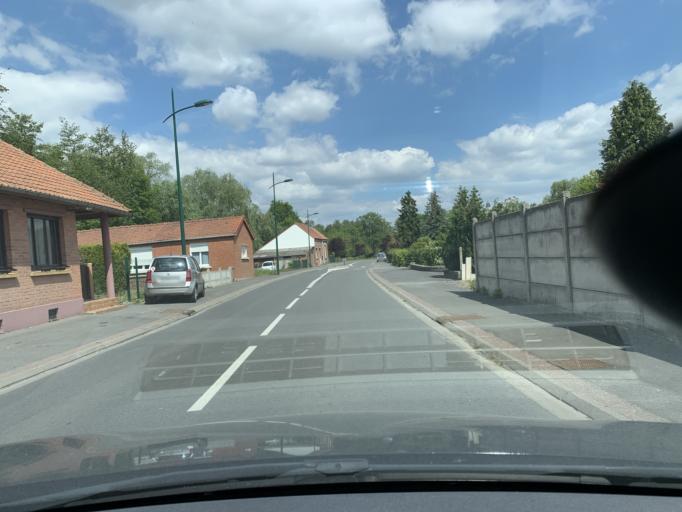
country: FR
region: Nord-Pas-de-Calais
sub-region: Departement du Nord
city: Arleux
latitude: 50.2702
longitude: 3.1000
